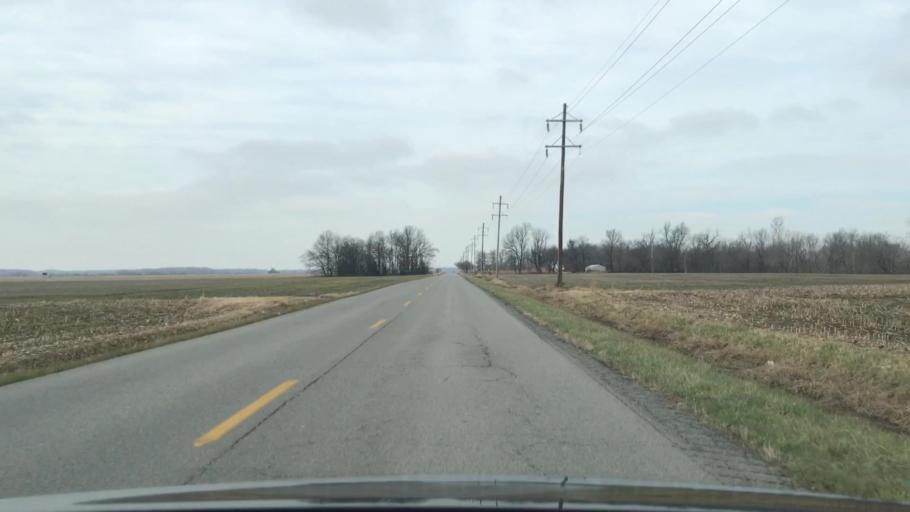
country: US
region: Kentucky
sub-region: McLean County
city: Calhoun
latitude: 37.5258
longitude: -87.2947
